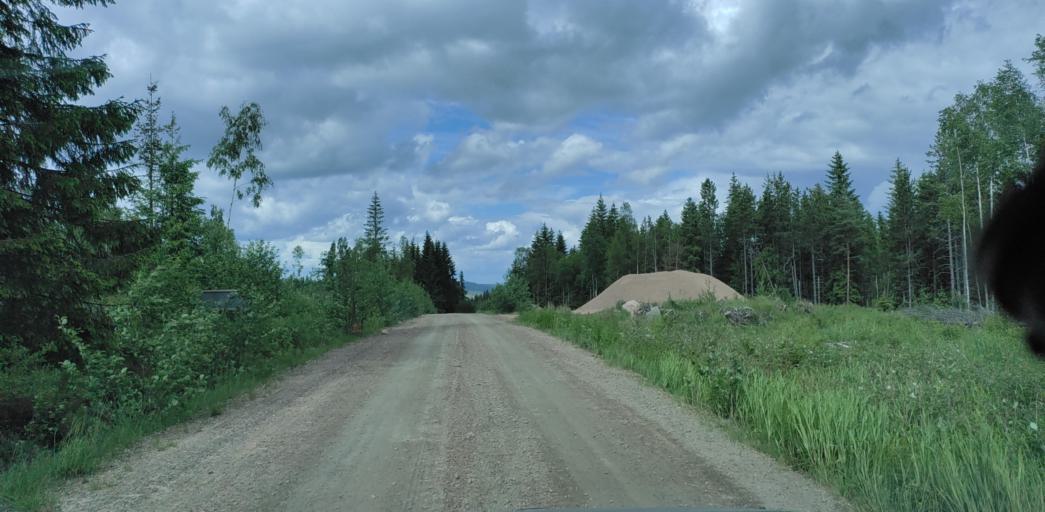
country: SE
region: Vaermland
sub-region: Munkfors Kommun
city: Munkfors
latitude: 59.9557
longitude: 13.4110
